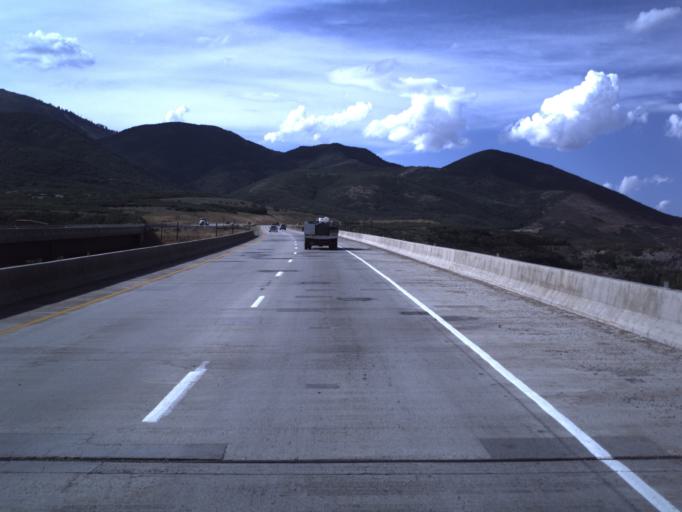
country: US
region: Utah
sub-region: Wasatch County
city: Heber
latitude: 40.5706
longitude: -111.4310
